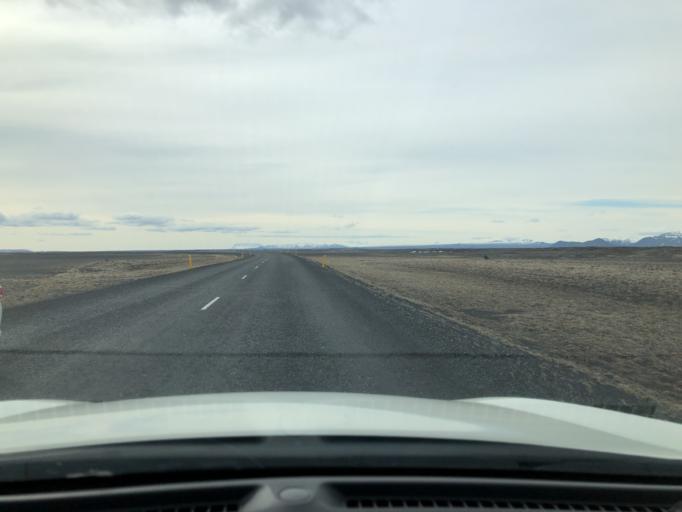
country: IS
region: Northeast
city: Laugar
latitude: 65.6848
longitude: -16.3843
